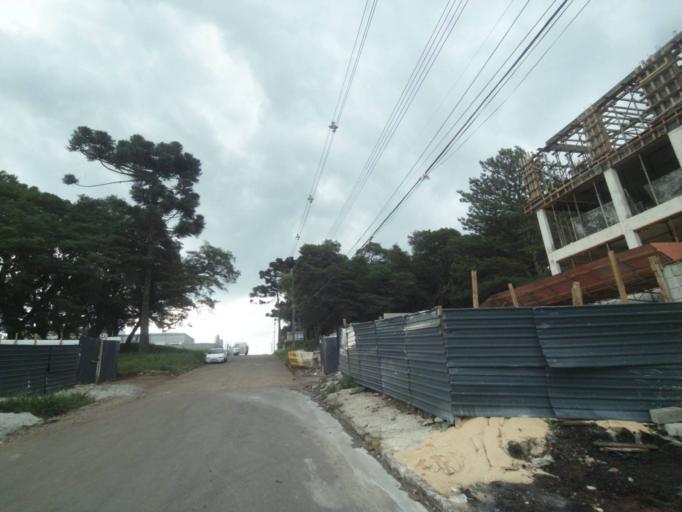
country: BR
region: Parana
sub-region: Curitiba
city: Curitiba
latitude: -25.4421
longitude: -49.3594
